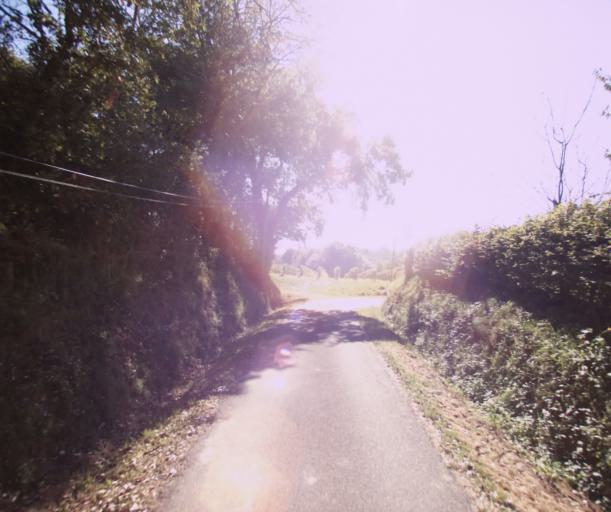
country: FR
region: Midi-Pyrenees
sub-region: Departement du Gers
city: Cazaubon
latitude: 43.9514
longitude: -0.0274
